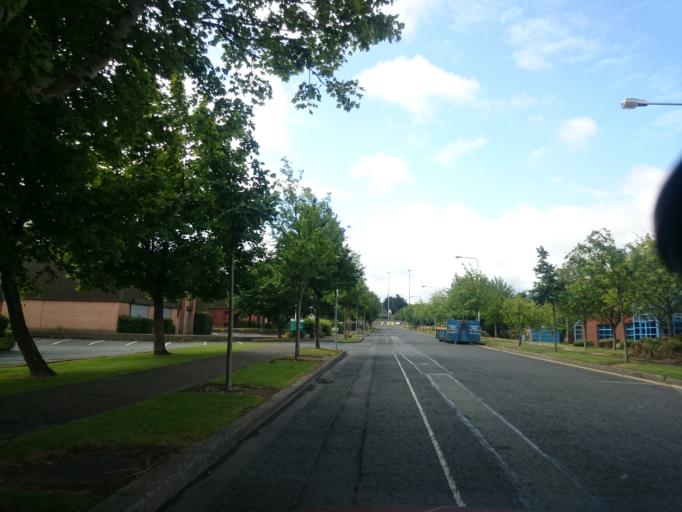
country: IE
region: Leinster
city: Sandyford
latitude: 53.2730
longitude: -6.2139
